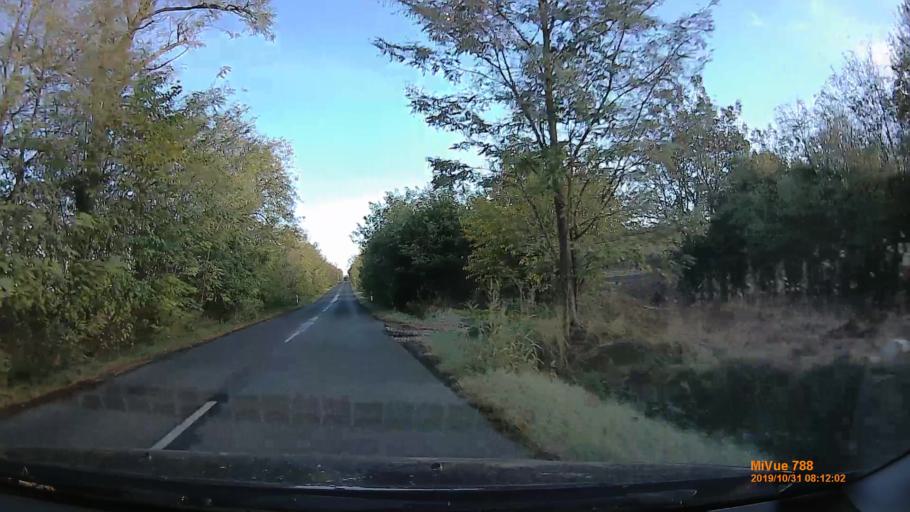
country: HU
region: Pest
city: Pilis
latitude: 47.3207
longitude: 19.5654
